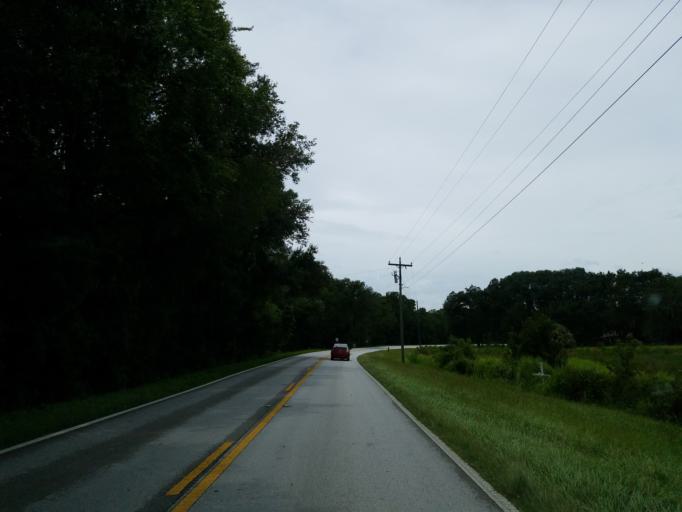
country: US
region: Florida
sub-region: Sumter County
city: Bushnell
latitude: 28.6691
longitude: -82.1832
